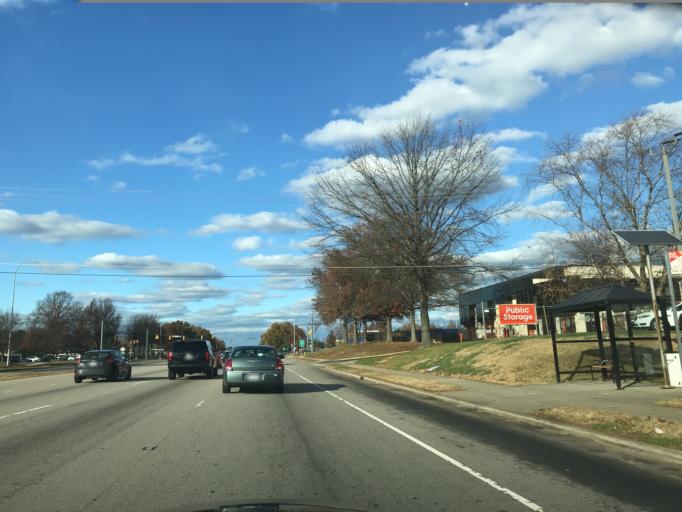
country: US
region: North Carolina
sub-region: Wake County
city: Raleigh
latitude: 35.8534
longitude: -78.5807
